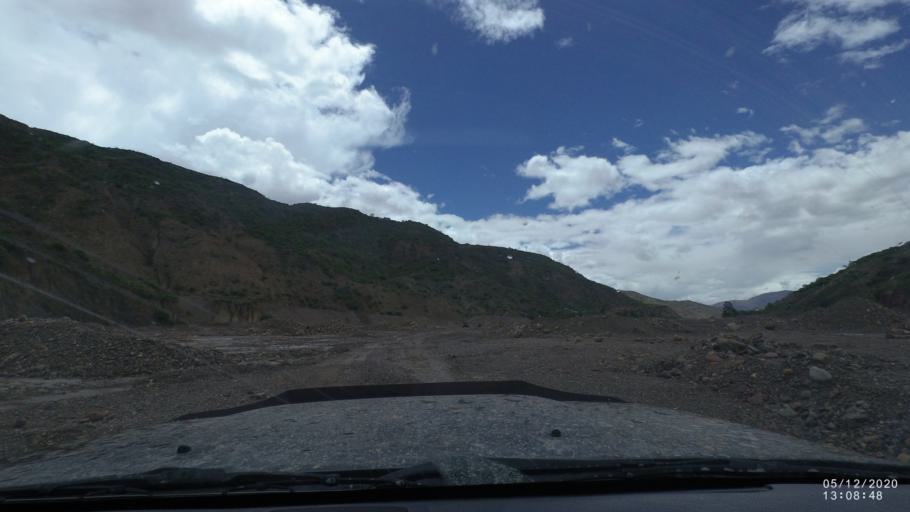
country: BO
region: Cochabamba
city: Sipe Sipe
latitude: -17.5621
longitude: -66.4541
